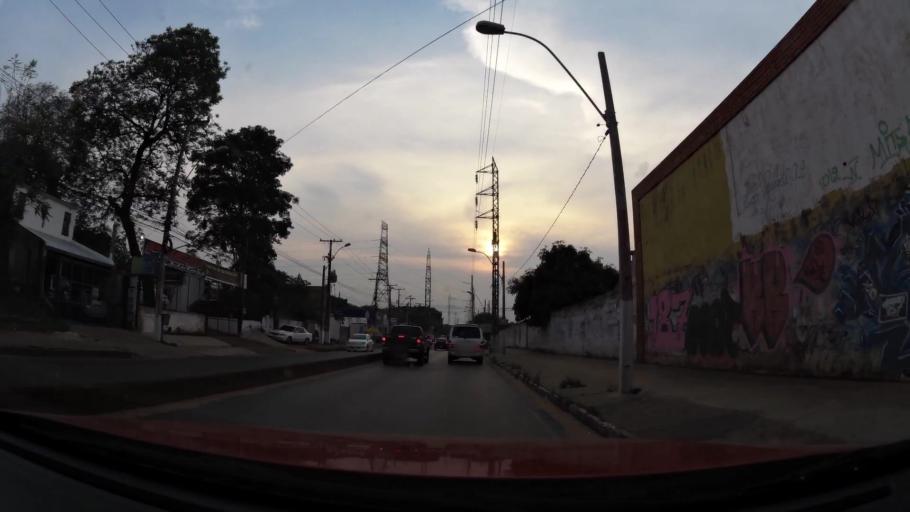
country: PY
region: Central
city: Lambare
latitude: -25.3431
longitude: -57.6094
